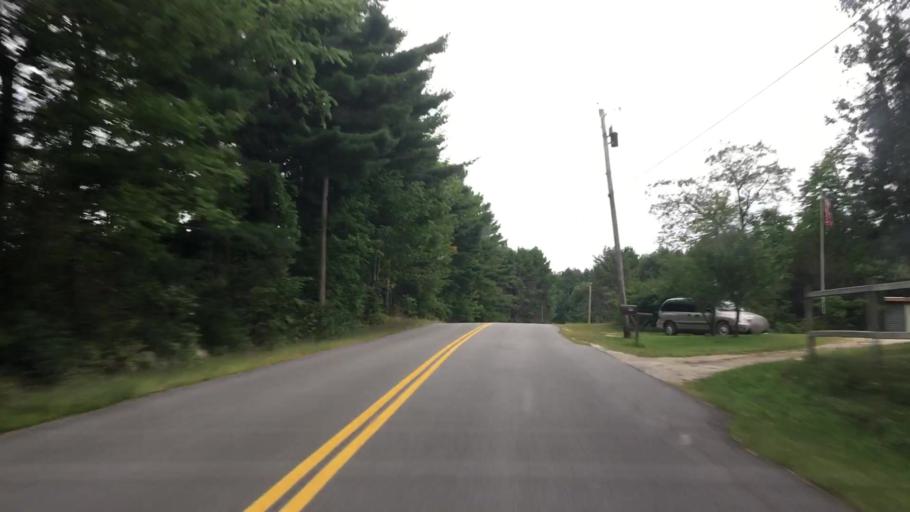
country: US
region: Maine
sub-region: Cumberland County
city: New Gloucester
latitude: 43.9154
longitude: -70.2431
